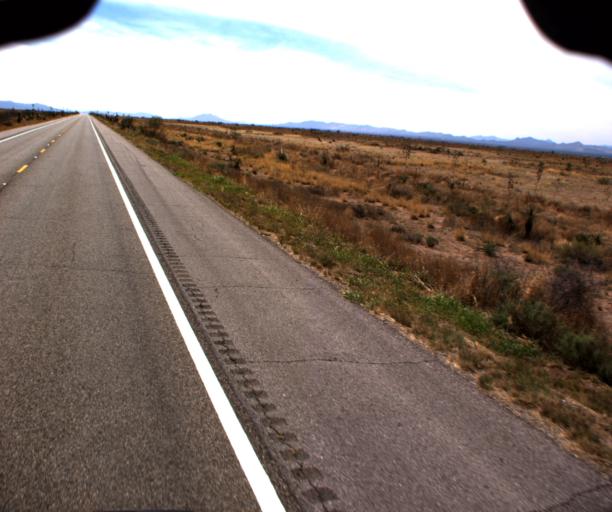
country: US
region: Arizona
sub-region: Cochise County
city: Pirtleville
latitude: 31.5471
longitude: -109.6604
